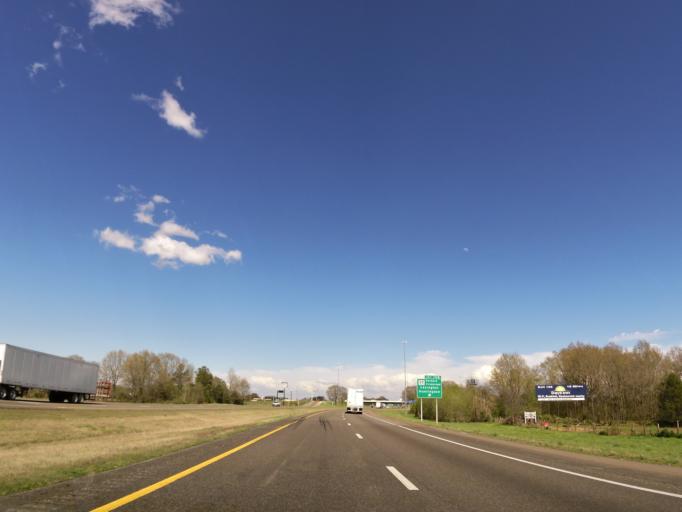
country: US
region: Tennessee
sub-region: Henderson County
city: Lexington
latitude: 35.7878
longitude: -88.3979
